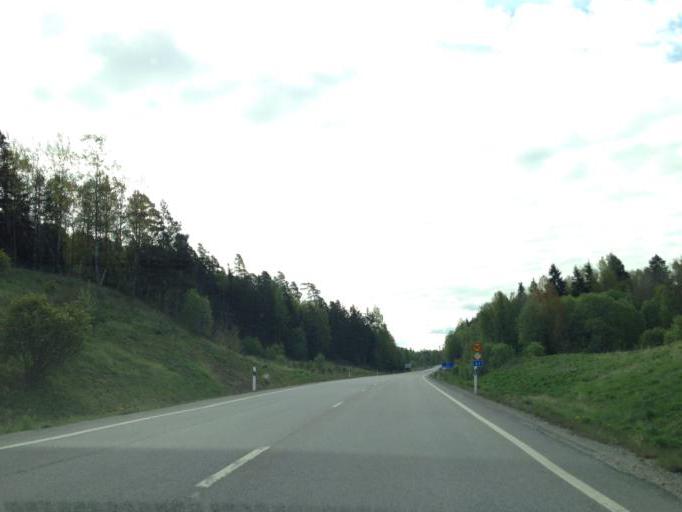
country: SE
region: Soedermanland
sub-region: Flens Kommun
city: Malmkoping
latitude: 59.1204
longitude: 16.7528
